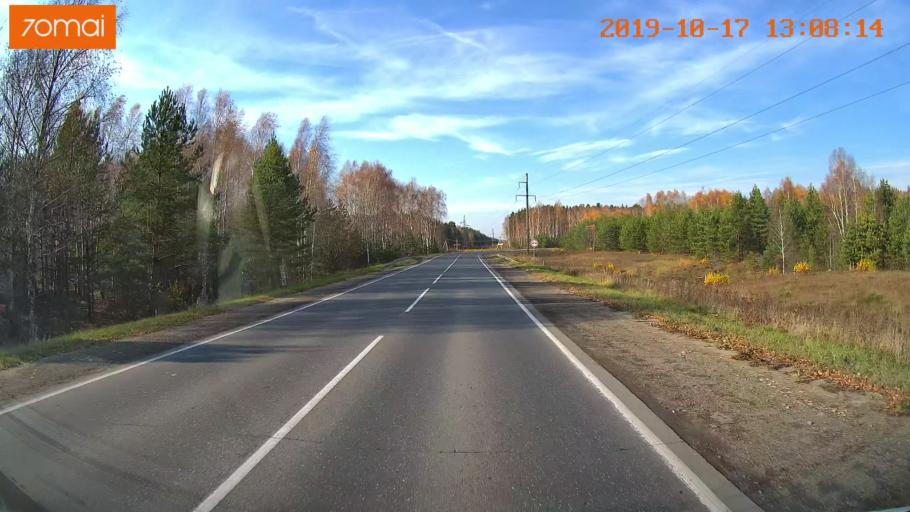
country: RU
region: Rjazan
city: Syntul
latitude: 54.9877
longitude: 41.2718
